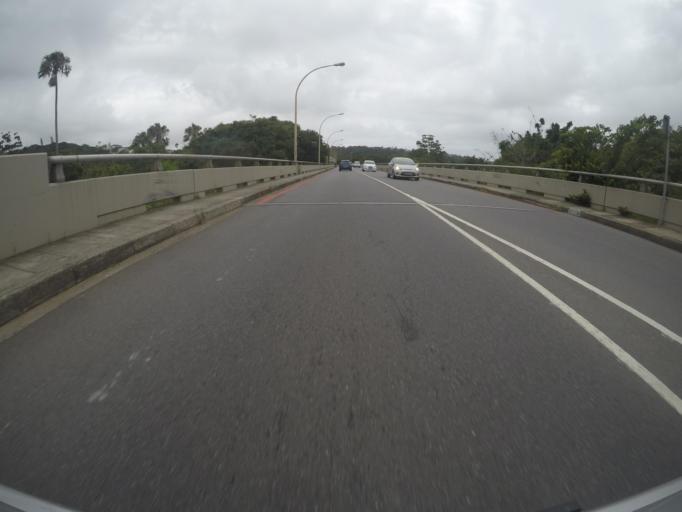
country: ZA
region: Eastern Cape
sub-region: Buffalo City Metropolitan Municipality
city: East London
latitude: -32.9738
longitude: 27.9242
